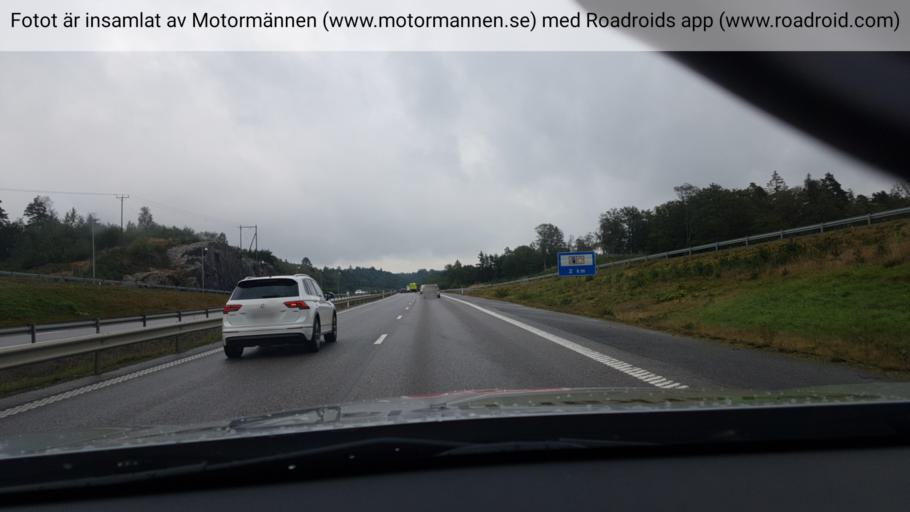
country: SE
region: Vaestra Goetaland
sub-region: Harryda Kommun
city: Landvetter
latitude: 57.6811
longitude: 12.1677
